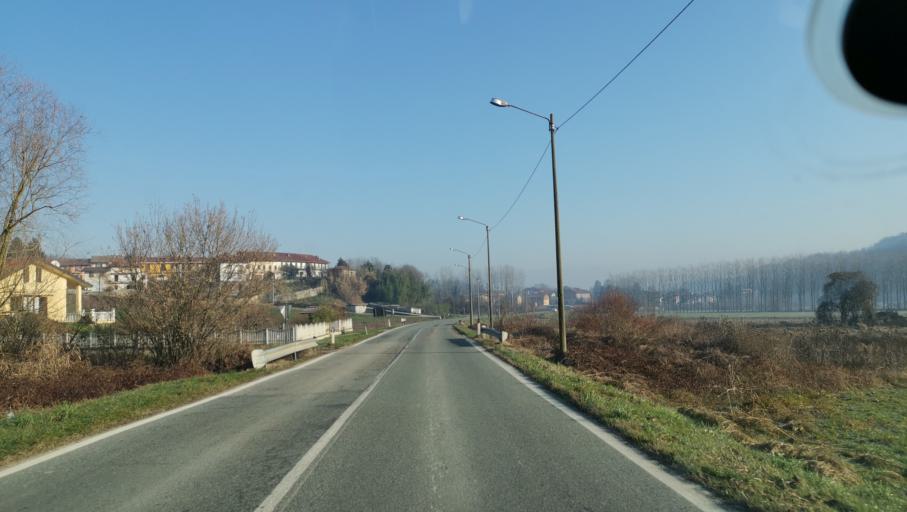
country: IT
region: Piedmont
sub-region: Provincia di Torino
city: San Sebastiano da Po
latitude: 45.1548
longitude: 7.9446
